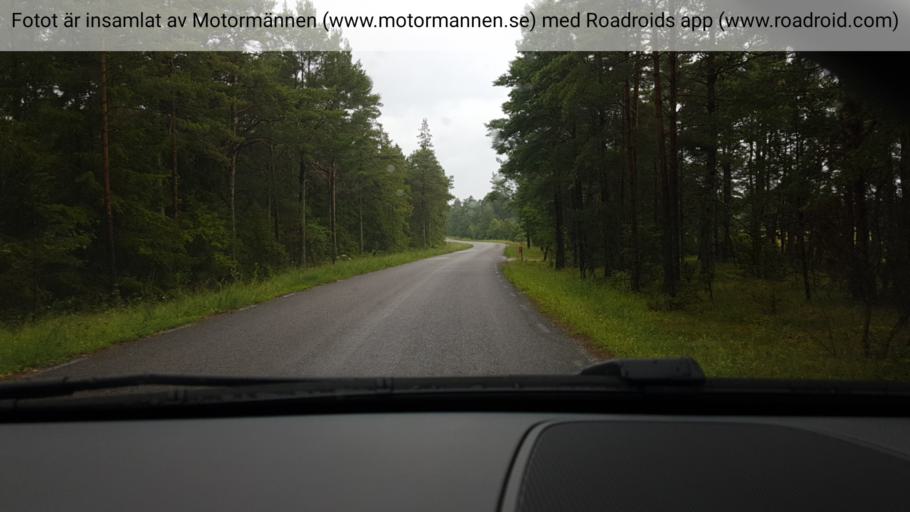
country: SE
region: Gotland
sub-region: Gotland
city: Slite
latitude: 57.8764
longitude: 18.7745
